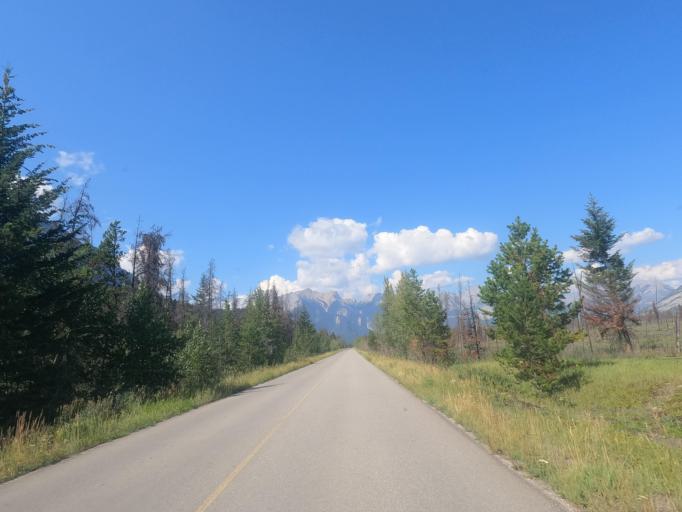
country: CA
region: Alberta
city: Jasper Park Lodge
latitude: 52.9781
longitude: -118.0681
